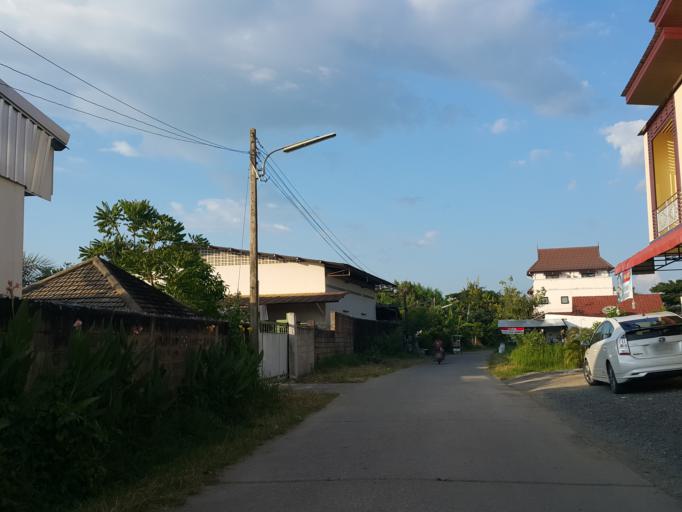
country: TH
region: Chiang Mai
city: San Kamphaeng
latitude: 18.7478
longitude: 99.1149
